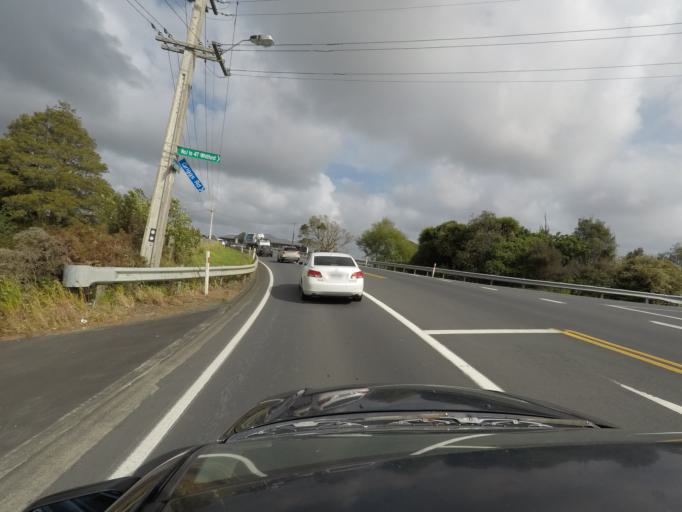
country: NZ
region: Auckland
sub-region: Auckland
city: Pakuranga
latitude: -36.9422
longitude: 174.9463
